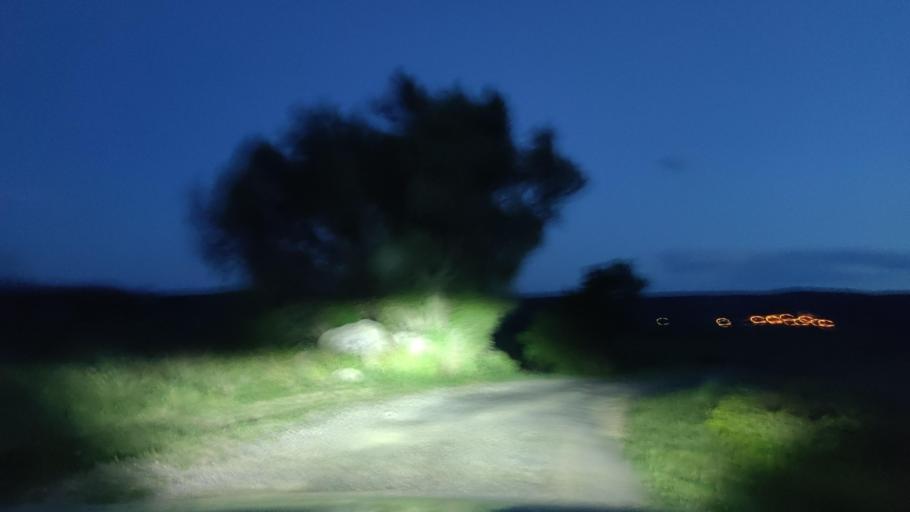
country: FR
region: Languedoc-Roussillon
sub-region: Departement des Pyrenees-Orientales
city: Estagel
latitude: 42.8709
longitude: 2.7292
